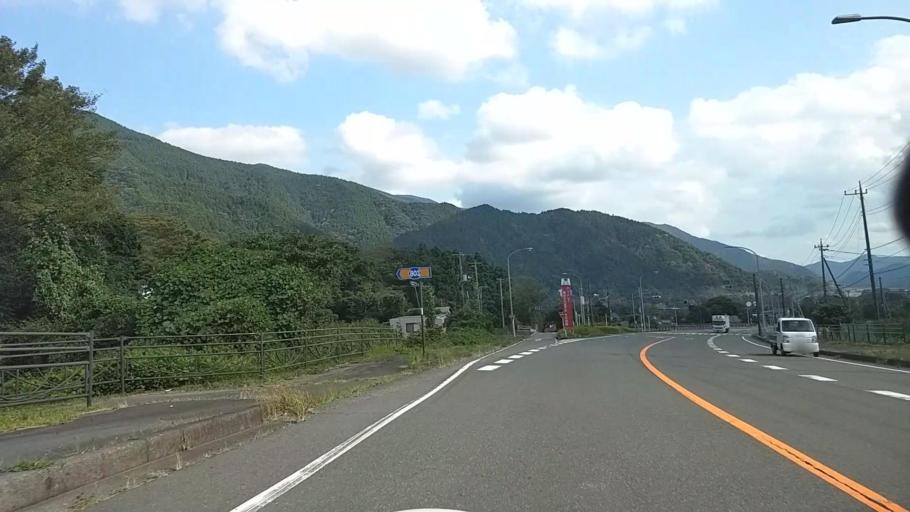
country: JP
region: Shizuoka
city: Fujinomiya
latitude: 35.3103
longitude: 138.4462
